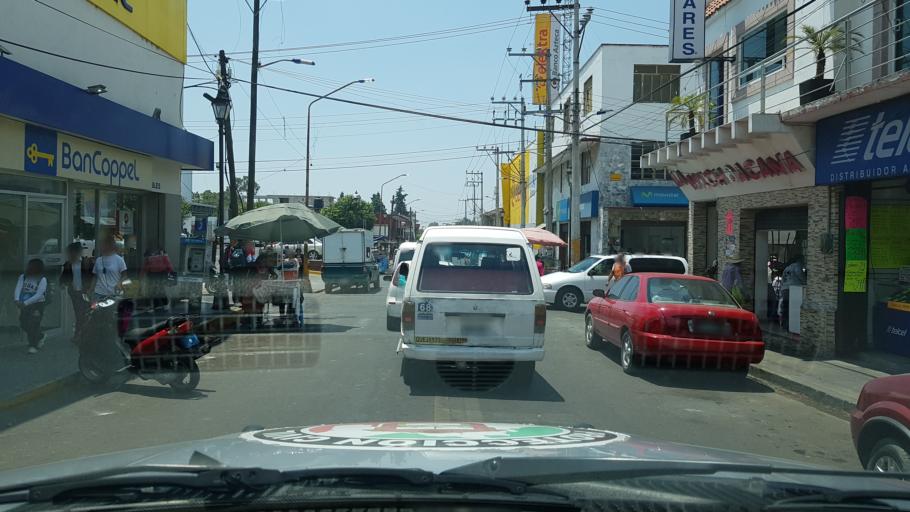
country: MX
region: Mexico
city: Ozumba de Alzate
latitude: 19.0356
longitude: -98.7976
